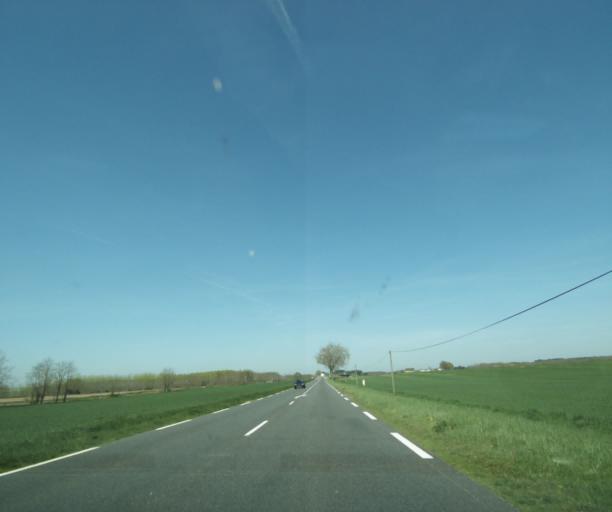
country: FR
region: Auvergne
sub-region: Departement de l'Allier
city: Trevol
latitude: 46.6701
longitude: 3.2380
